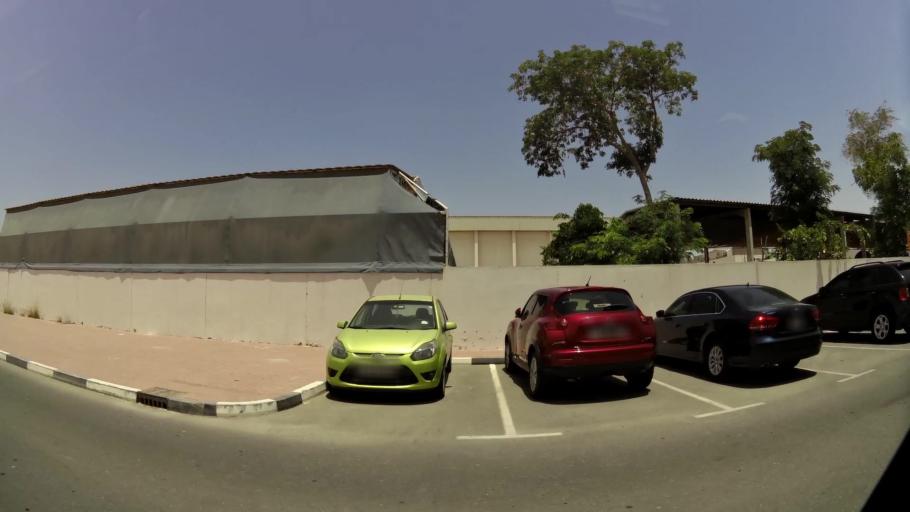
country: AE
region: Dubai
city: Dubai
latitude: 25.1890
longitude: 55.2530
